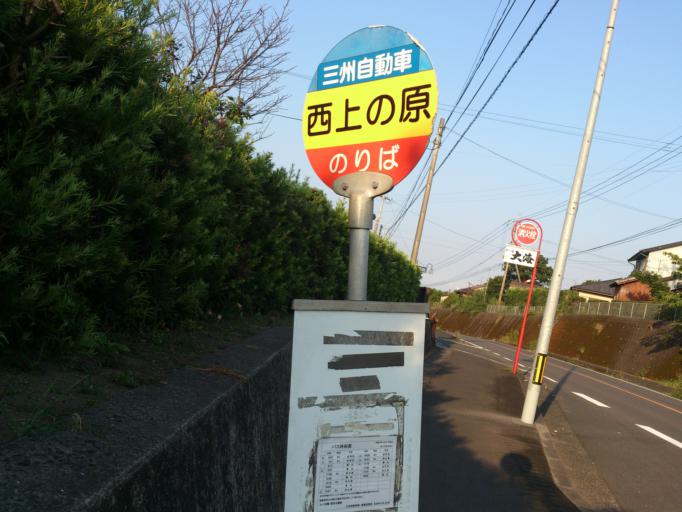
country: JP
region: Kagoshima
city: Kanoya
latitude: 31.3430
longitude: 130.9308
